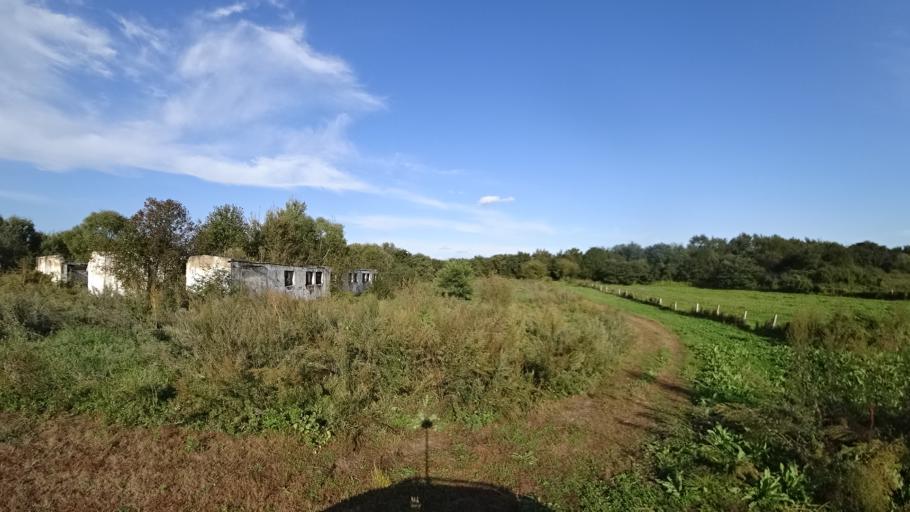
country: RU
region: Amur
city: Arkhara
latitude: 49.3488
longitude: 130.1065
